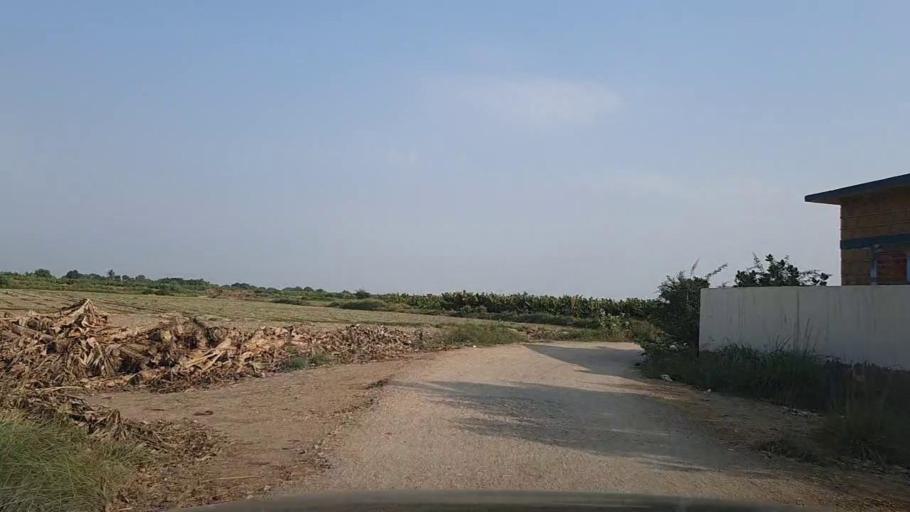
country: PK
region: Sindh
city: Thatta
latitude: 24.6442
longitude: 67.9401
